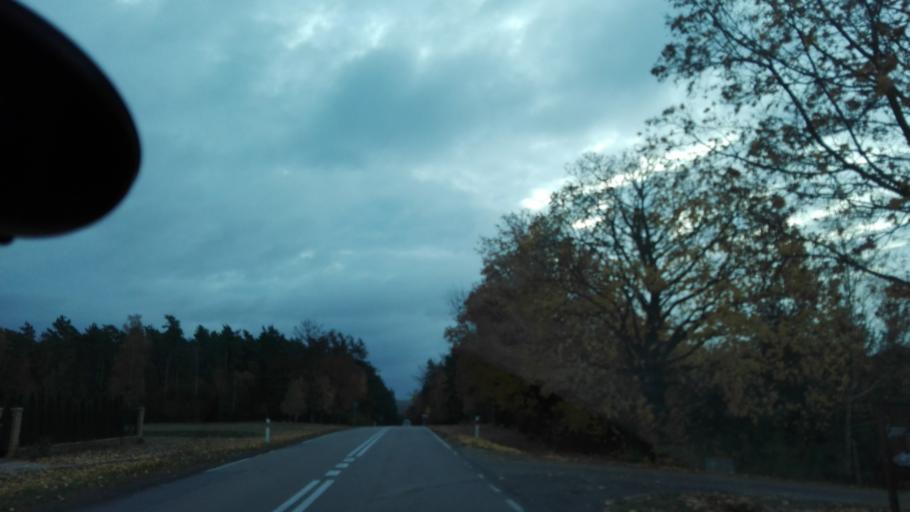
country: PL
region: Lublin Voivodeship
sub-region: Powiat pulawski
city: Pulawy
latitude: 51.4469
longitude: 21.8983
